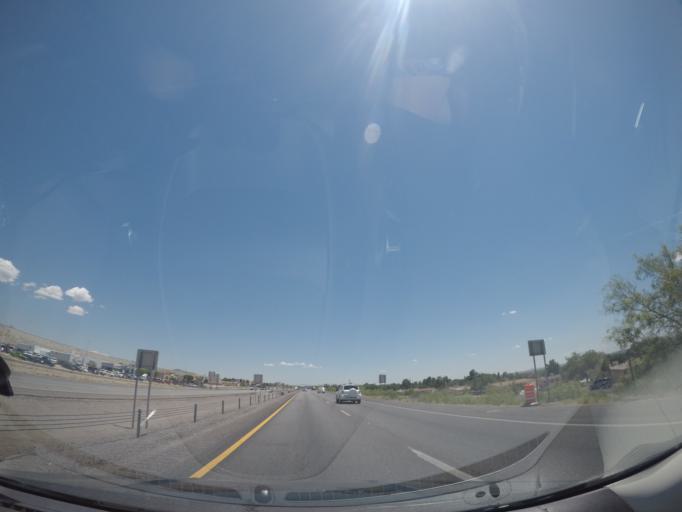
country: US
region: New Mexico
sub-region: Dona Ana County
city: Las Cruces
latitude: 32.3306
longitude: -106.7576
